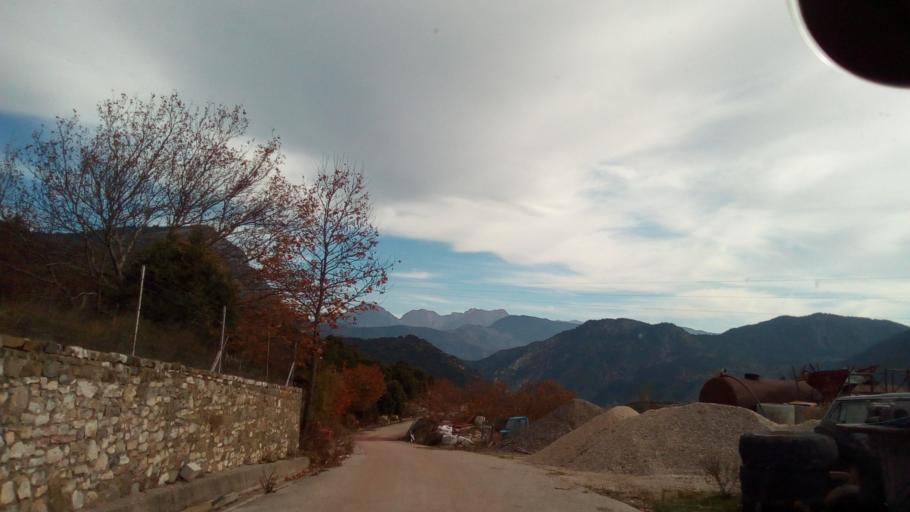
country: GR
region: West Greece
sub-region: Nomos Aitolias kai Akarnanias
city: Thermo
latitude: 38.6750
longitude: 21.8925
